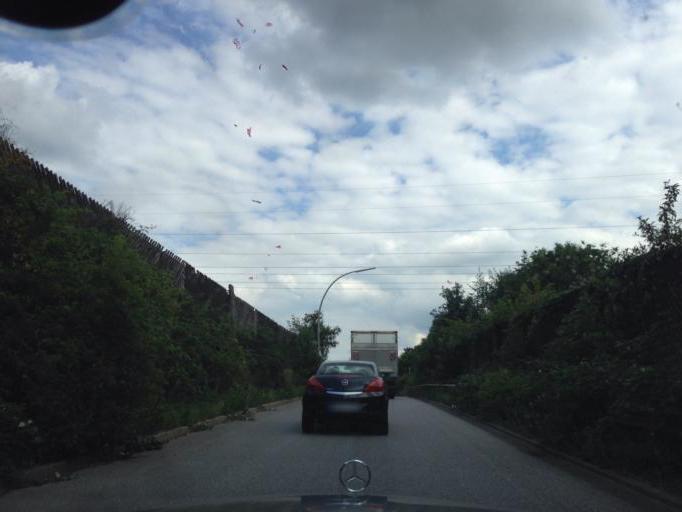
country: DE
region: Hamburg
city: Marienthal
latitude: 53.5444
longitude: 10.0842
